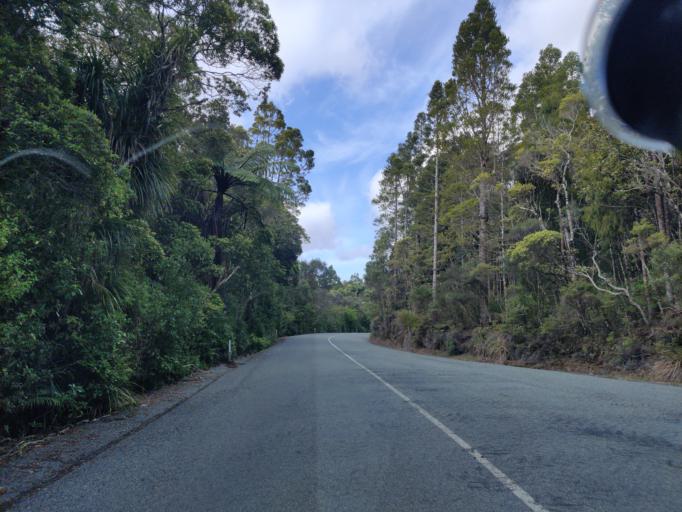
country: NZ
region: Northland
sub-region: Far North District
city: Waimate North
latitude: -35.6076
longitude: 173.5366
